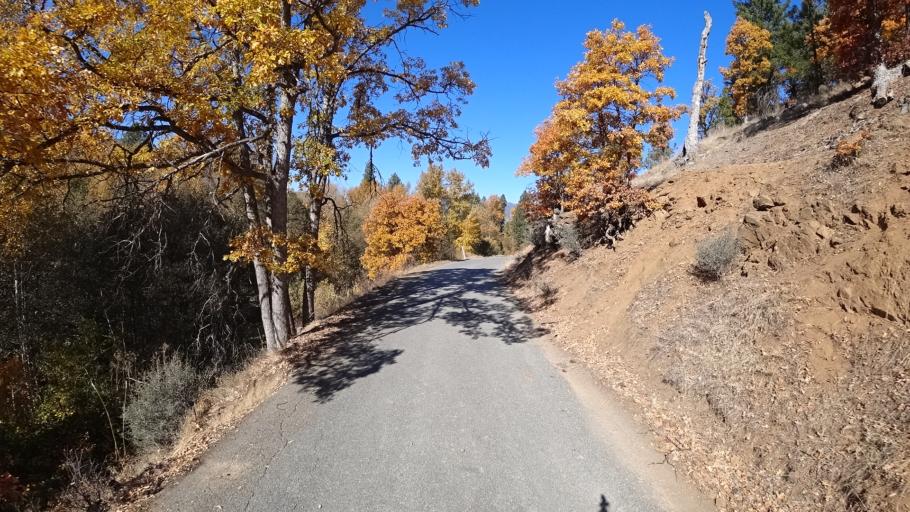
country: US
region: California
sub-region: Siskiyou County
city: Yreka
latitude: 41.6087
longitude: -122.9628
